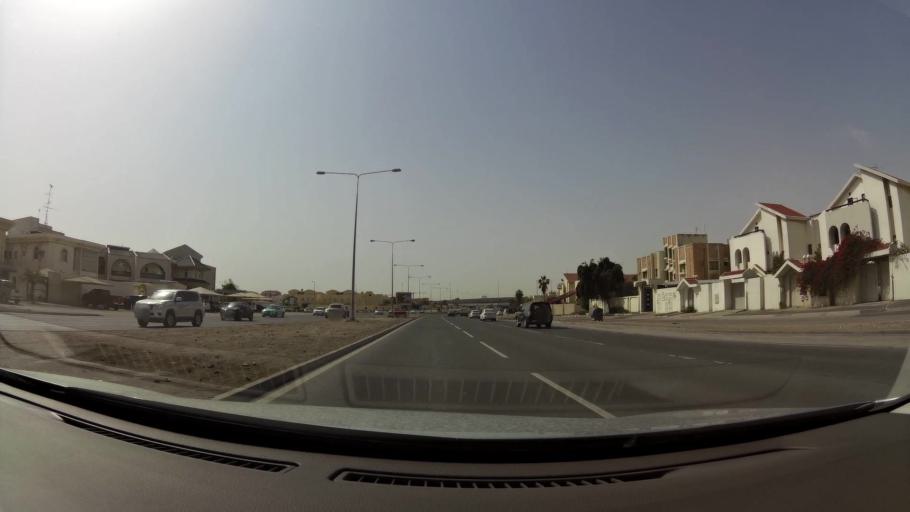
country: QA
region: Baladiyat ad Dawhah
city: Doha
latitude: 25.2422
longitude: 51.5240
